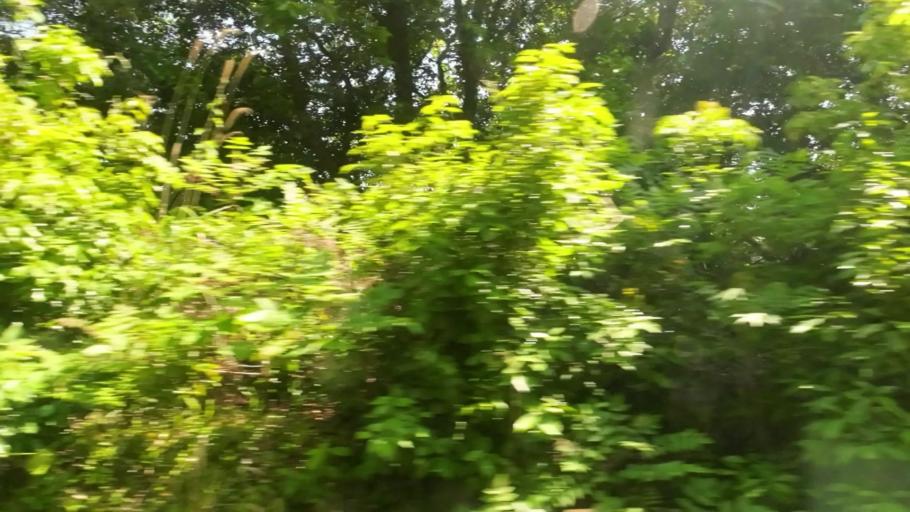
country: JP
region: Ehime
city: Niihama
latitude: 33.9685
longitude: 133.3579
